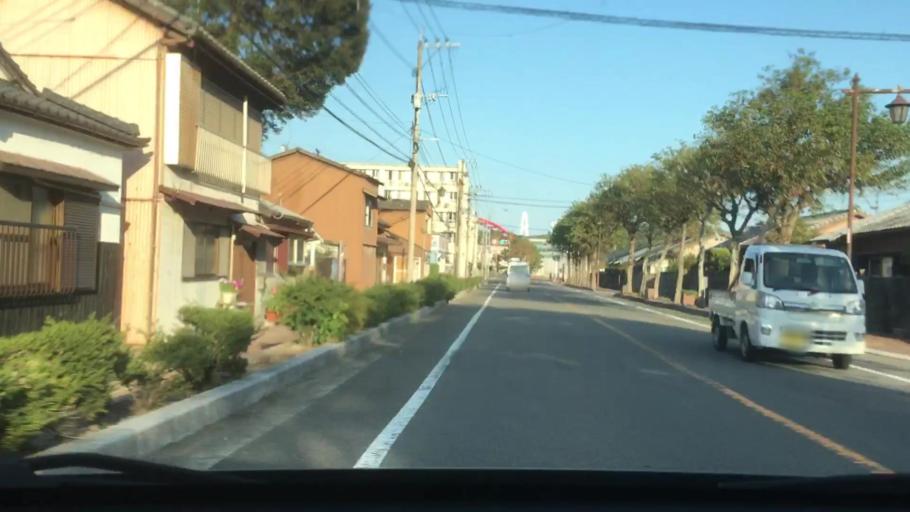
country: JP
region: Nagasaki
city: Sasebo
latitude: 33.0355
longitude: 129.6209
